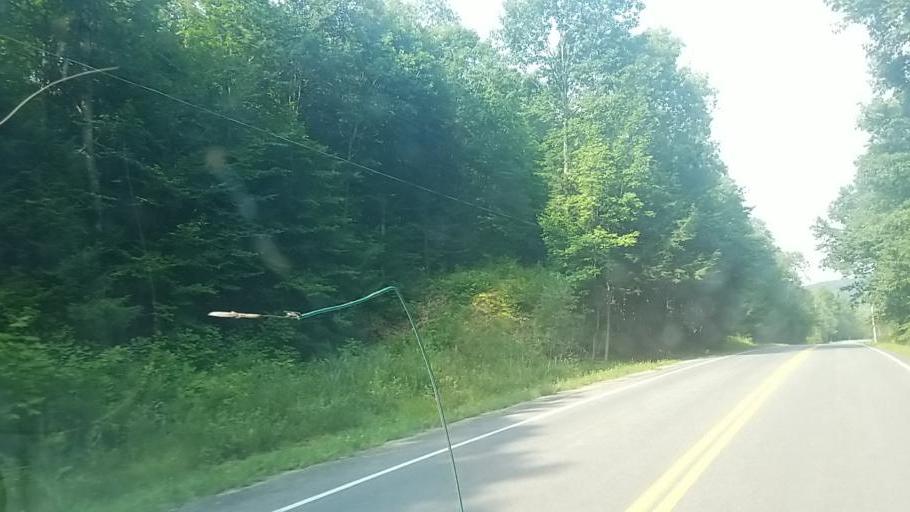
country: US
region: New York
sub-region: Fulton County
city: Gloversville
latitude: 43.1022
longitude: -74.3085
